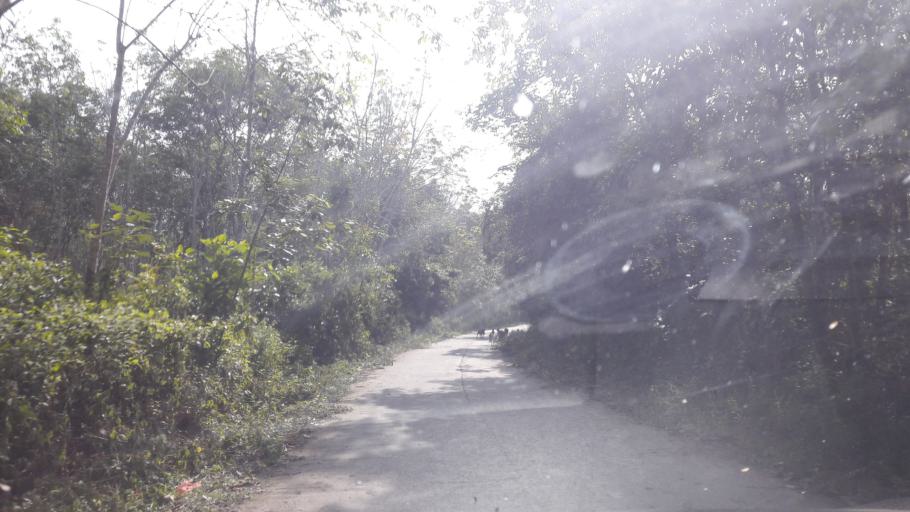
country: ID
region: South Sumatra
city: Gunungmenang
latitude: -3.1063
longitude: 103.9823
